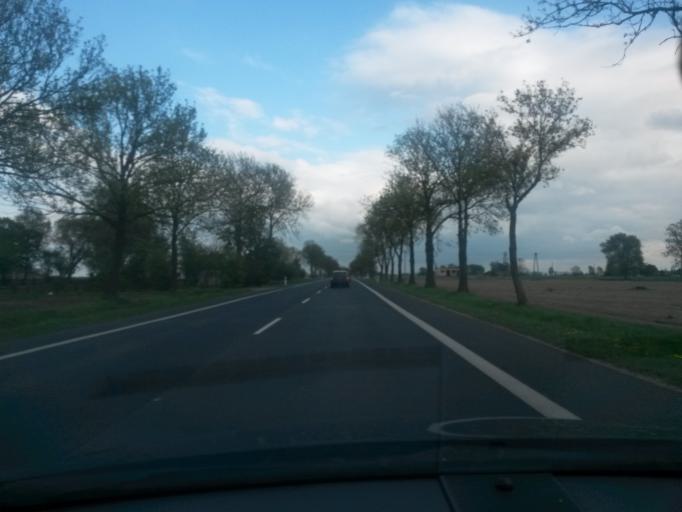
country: PL
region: Masovian Voivodeship
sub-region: Powiat plocki
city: Drobin
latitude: 52.7694
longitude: 19.9309
